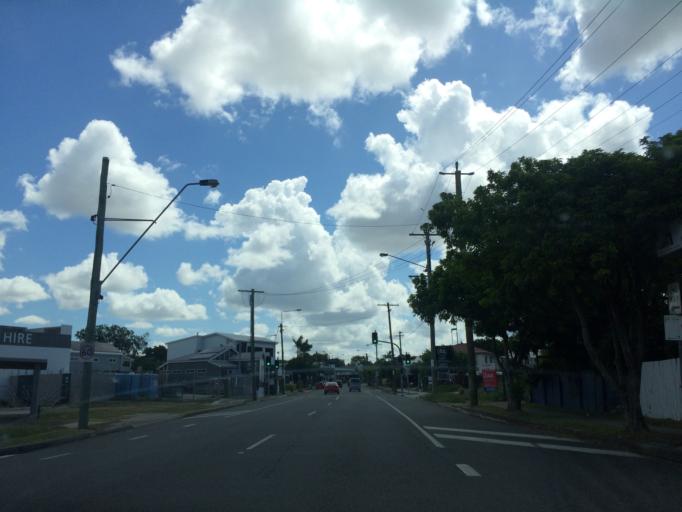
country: AU
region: Queensland
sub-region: Brisbane
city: Woolloongabba
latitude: -27.4878
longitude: 153.0501
